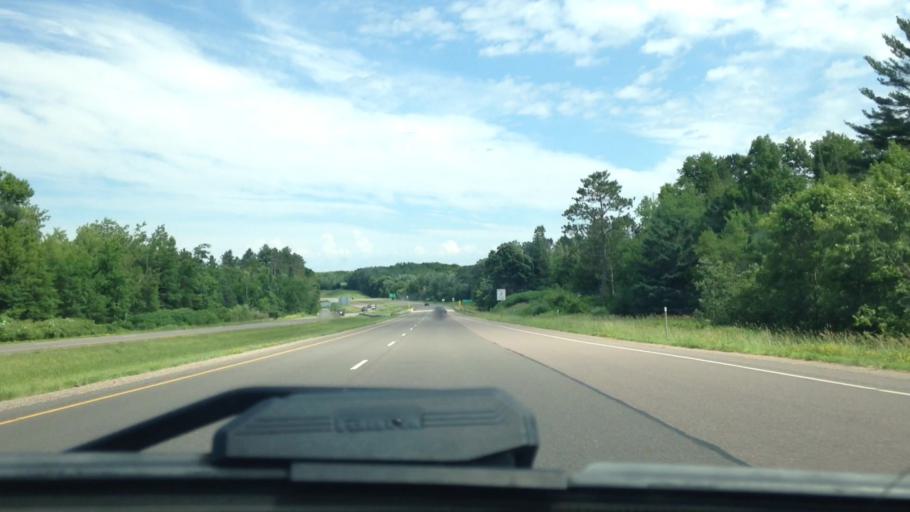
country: US
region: Wisconsin
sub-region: Washburn County
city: Spooner
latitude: 45.8217
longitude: -91.8559
